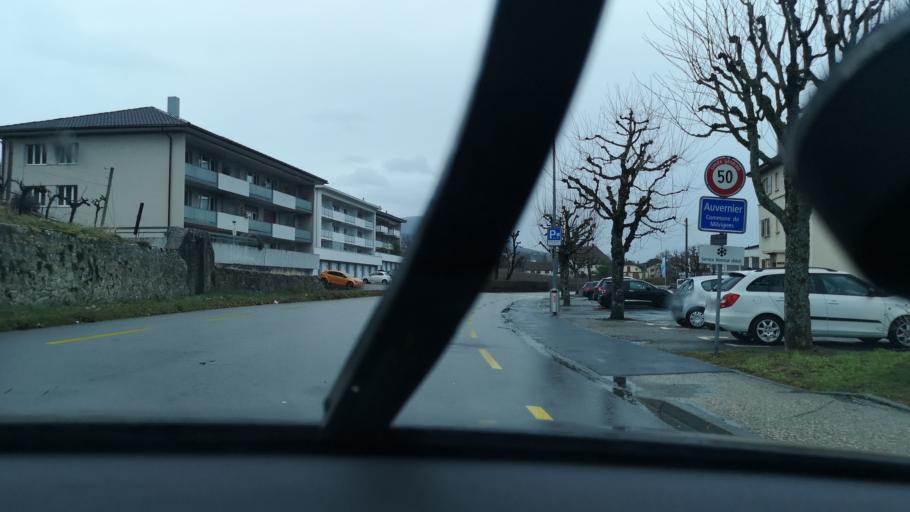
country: CH
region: Neuchatel
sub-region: Boudry District
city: Auvernier
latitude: 46.9726
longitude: 6.8722
